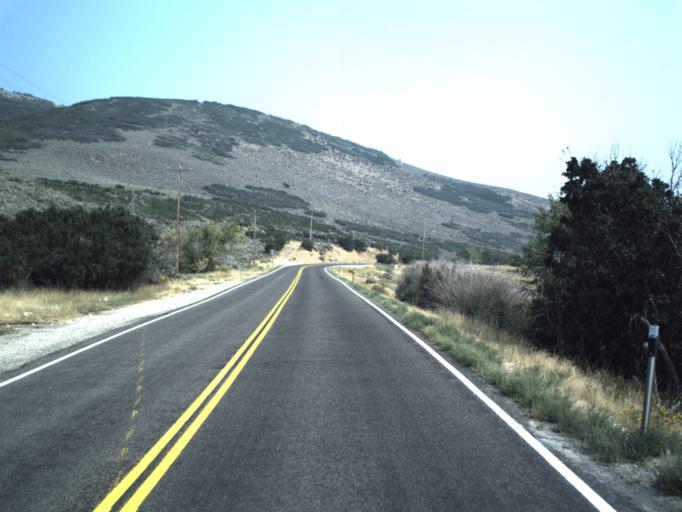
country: US
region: Utah
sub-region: Summit County
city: Kamas
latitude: 40.6405
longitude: -111.2646
